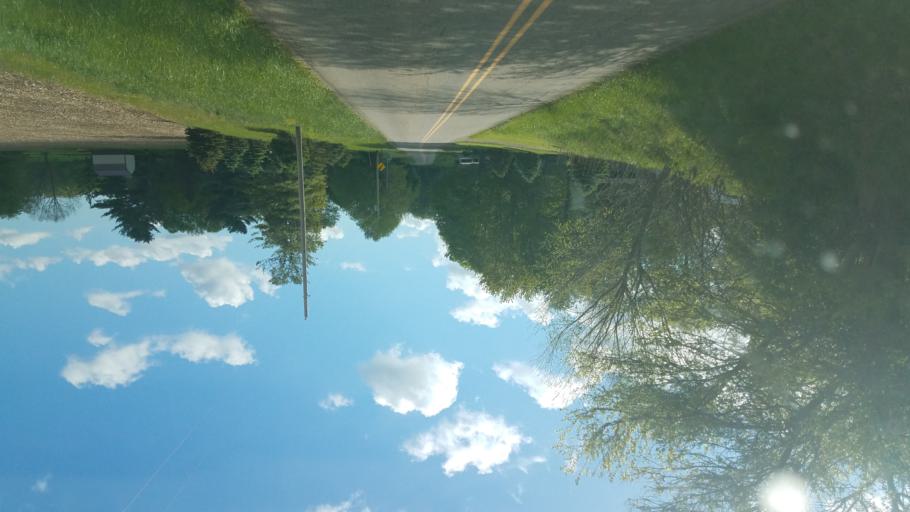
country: US
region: Ohio
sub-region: Knox County
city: Danville
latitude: 40.4954
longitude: -82.3554
